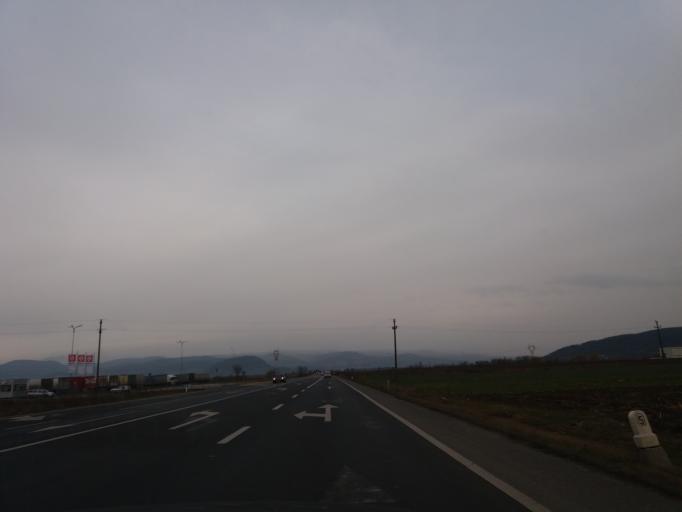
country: RO
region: Hunedoara
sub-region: Comuna Bacia
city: Bacia
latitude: 45.8121
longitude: 23.0182
